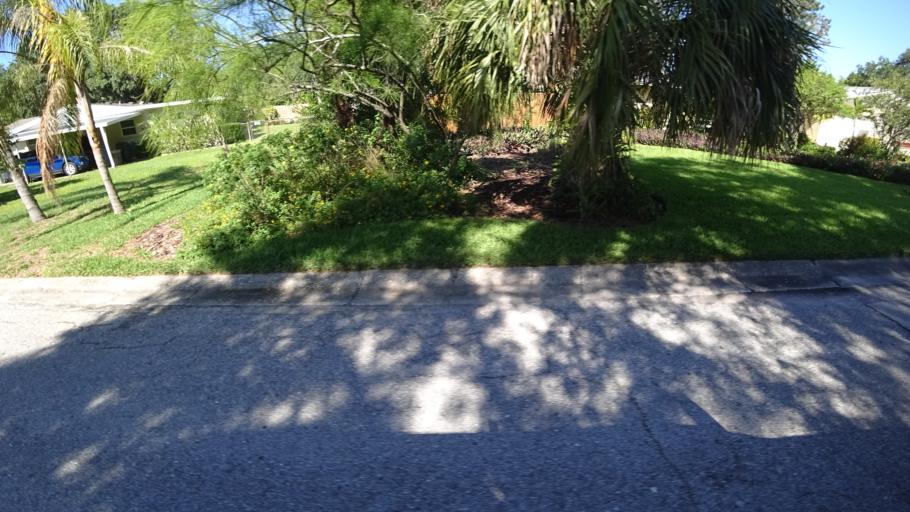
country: US
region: Florida
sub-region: Manatee County
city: West Bradenton
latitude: 27.4749
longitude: -82.6113
